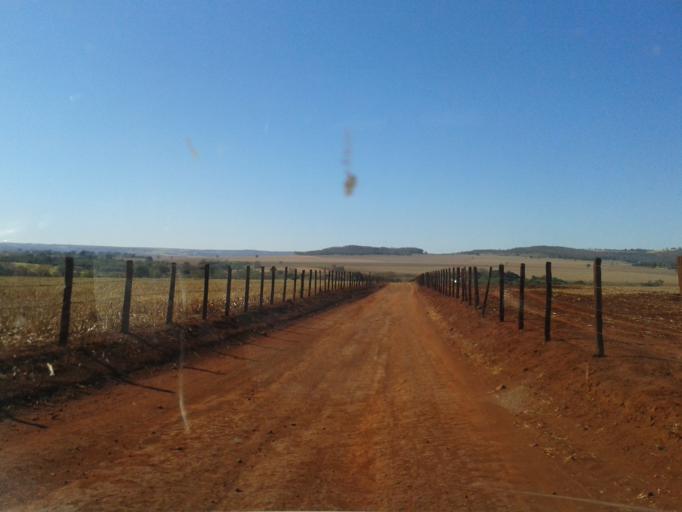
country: BR
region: Minas Gerais
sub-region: Centralina
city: Centralina
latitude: -18.5852
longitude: -49.1870
